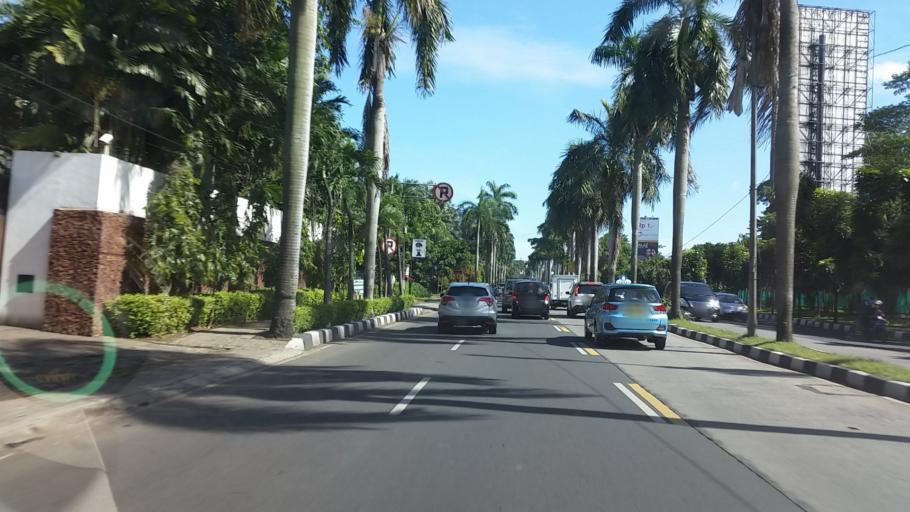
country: ID
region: Banten
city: South Tangerang
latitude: -6.2742
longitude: 106.7824
